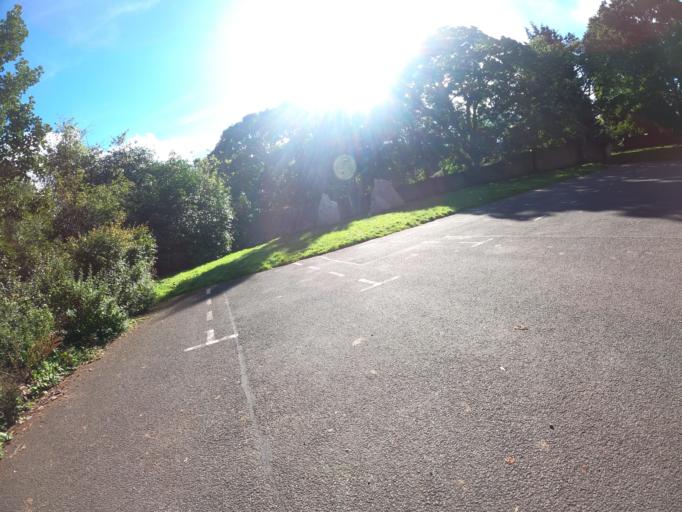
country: GB
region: Scotland
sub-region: Fife
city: Aberdour
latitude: 55.9775
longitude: -3.2982
